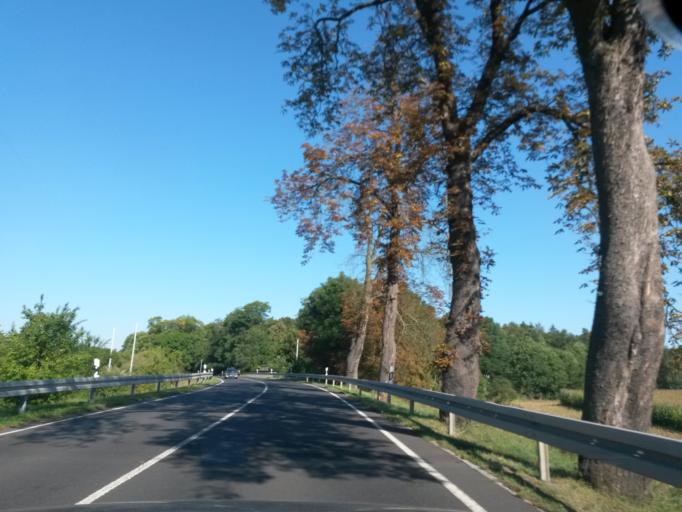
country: DE
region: Brandenburg
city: Angermunde
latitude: 53.0568
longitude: 13.9746
